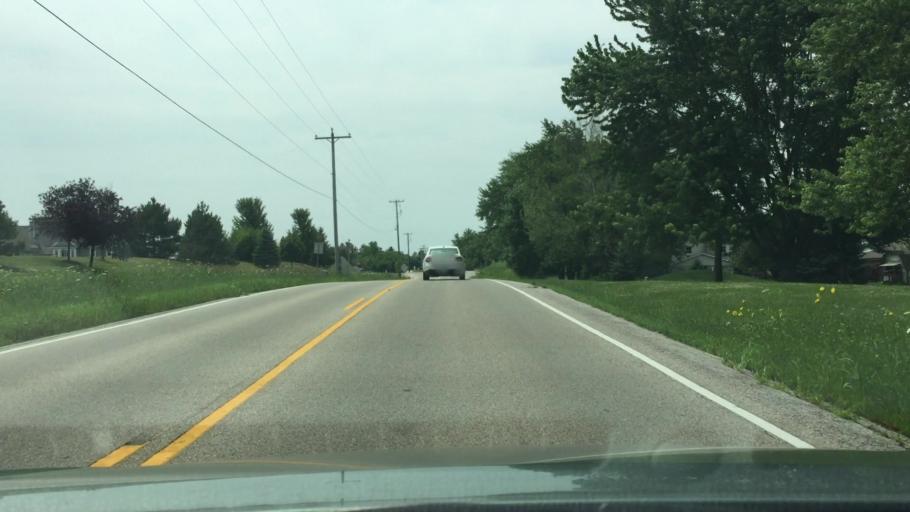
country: US
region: Wisconsin
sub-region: Waukesha County
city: Merton
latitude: 43.1382
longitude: -88.3074
